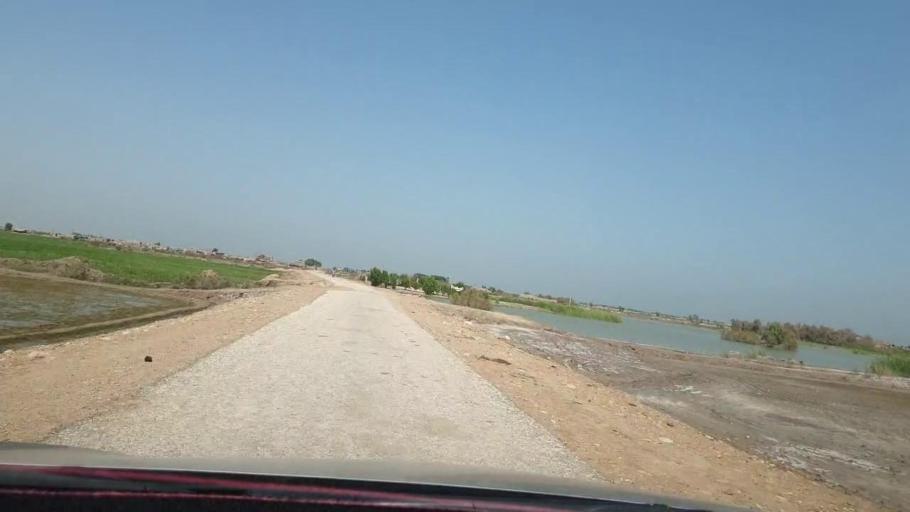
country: PK
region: Sindh
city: Warah
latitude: 27.5721
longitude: 67.7559
